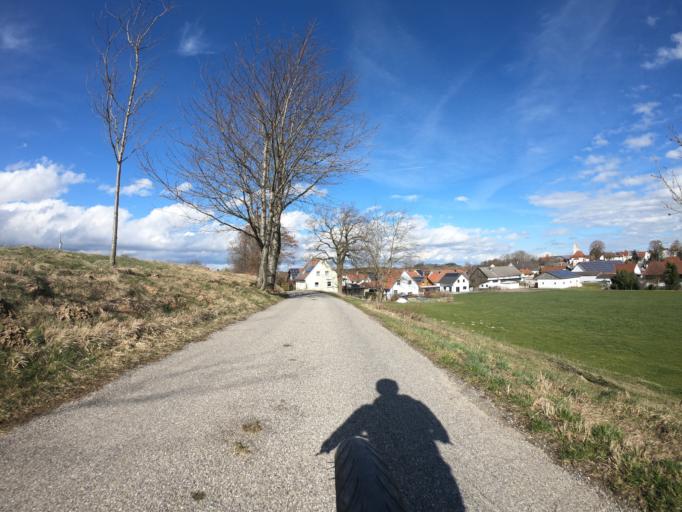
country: DE
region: Bavaria
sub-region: Upper Bavaria
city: Landsberied
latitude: 48.1785
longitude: 11.1833
